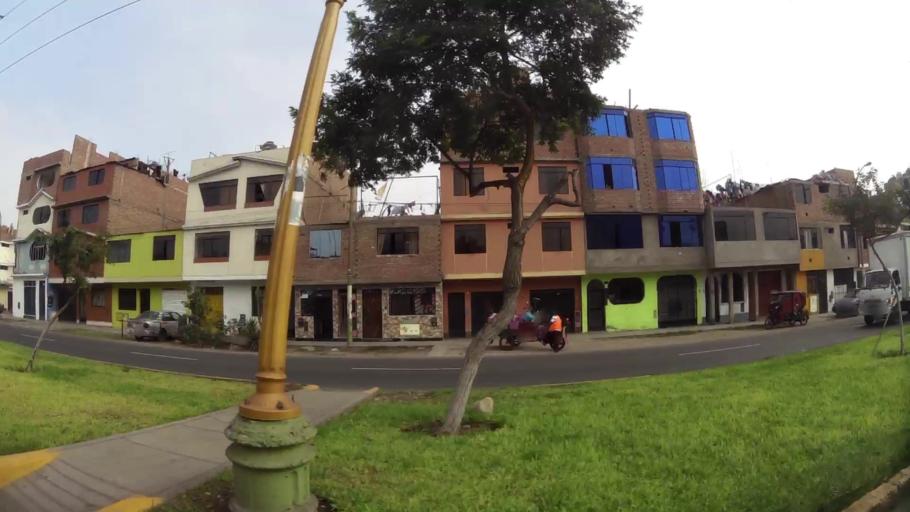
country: PE
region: Callao
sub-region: Callao
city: Callao
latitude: -12.0219
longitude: -77.0952
